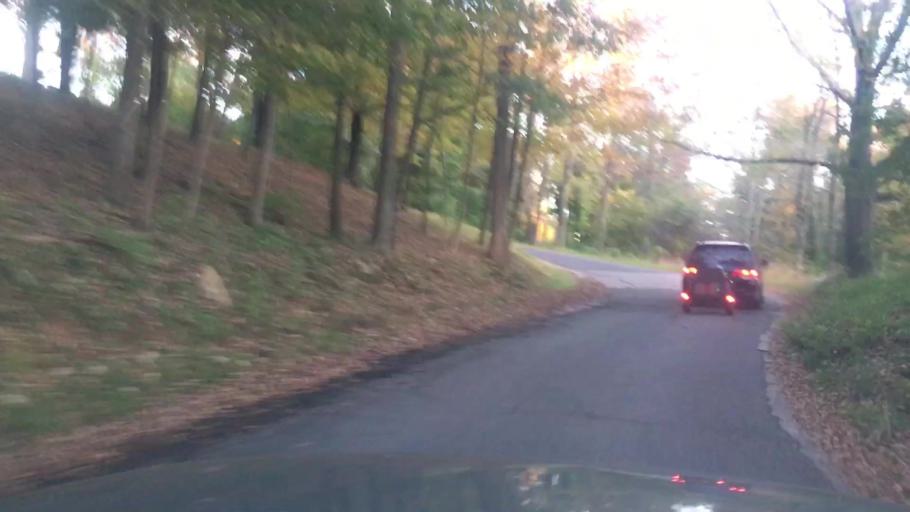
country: US
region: Massachusetts
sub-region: Worcester County
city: Charlton
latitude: 42.1247
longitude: -72.0004
